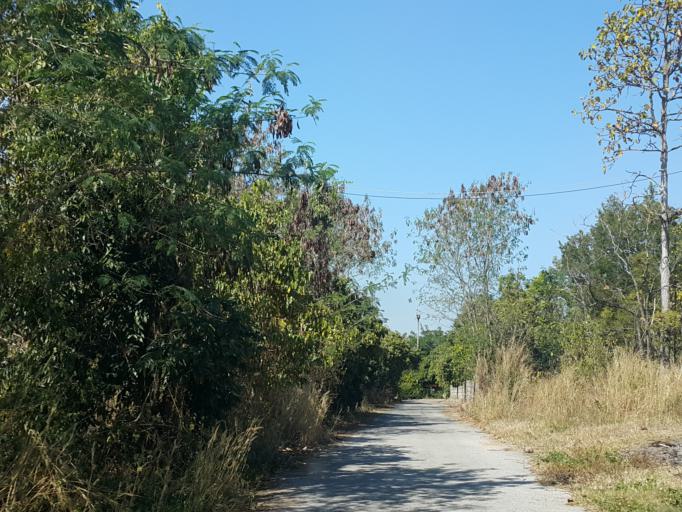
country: TH
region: Chiang Mai
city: Mae Taeng
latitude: 19.0348
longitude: 98.9844
